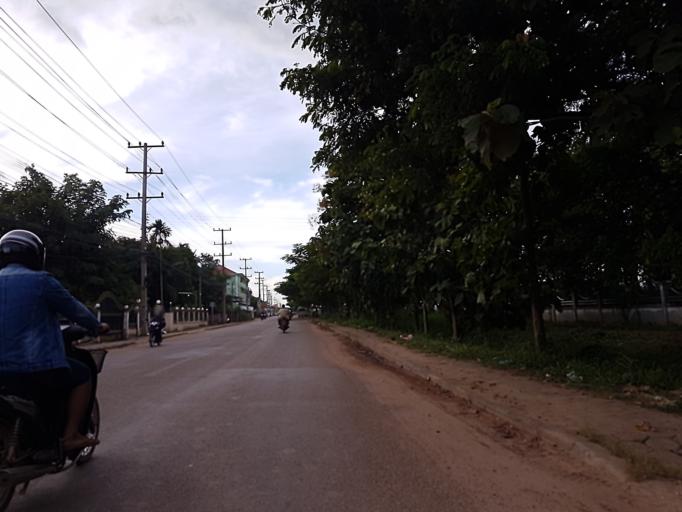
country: LA
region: Vientiane
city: Vientiane
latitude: 17.9886
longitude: 102.5770
